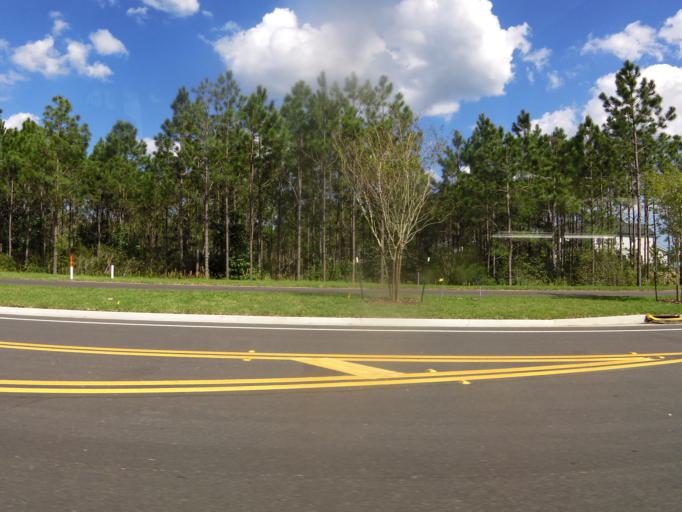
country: US
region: Florida
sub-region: Saint Johns County
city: Palm Valley
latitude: 30.1976
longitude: -81.5079
